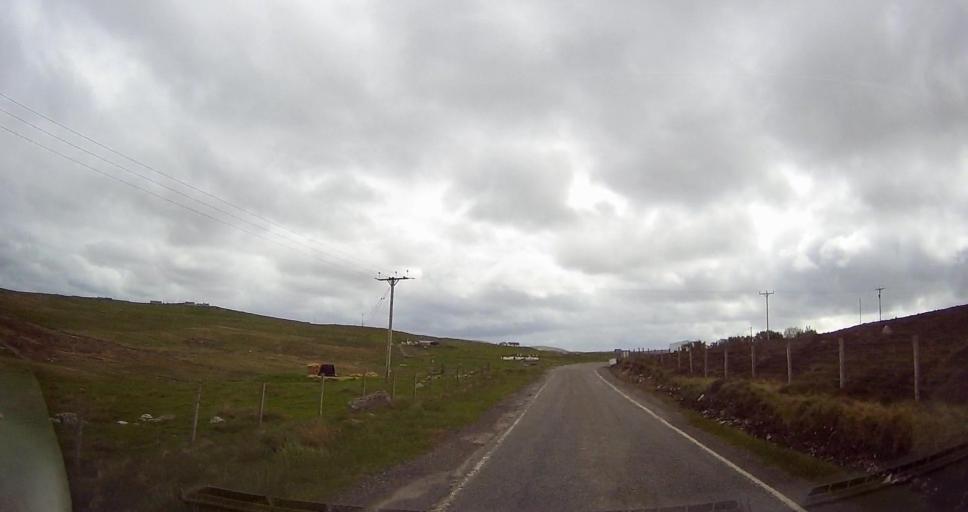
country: GB
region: Scotland
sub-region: Shetland Islands
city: Sandwick
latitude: 60.2452
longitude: -1.5114
